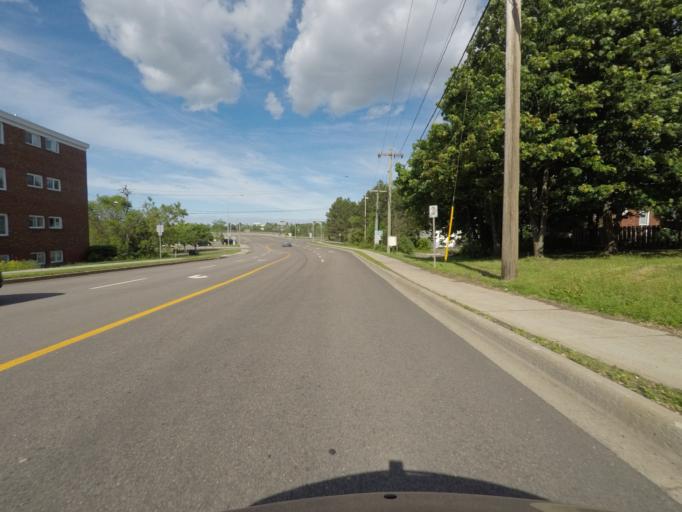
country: CA
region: New Brunswick
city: Moncton
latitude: 46.1043
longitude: -64.7966
